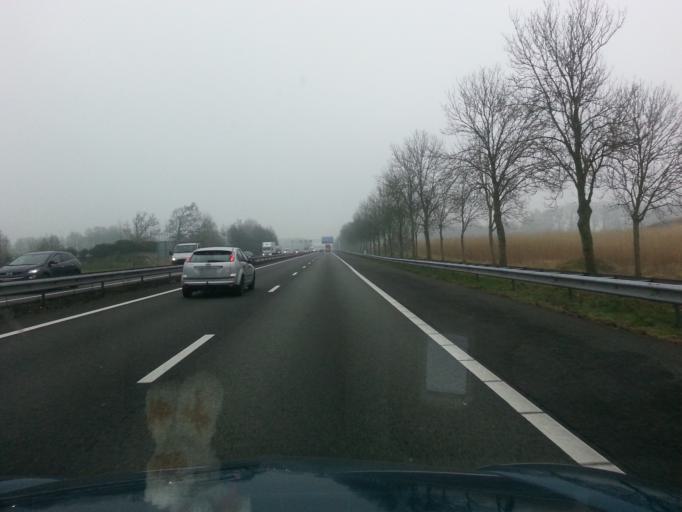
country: NL
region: Gelderland
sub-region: Gemeente Zevenaar
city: Zevenaar
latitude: 51.9237
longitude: 6.1209
